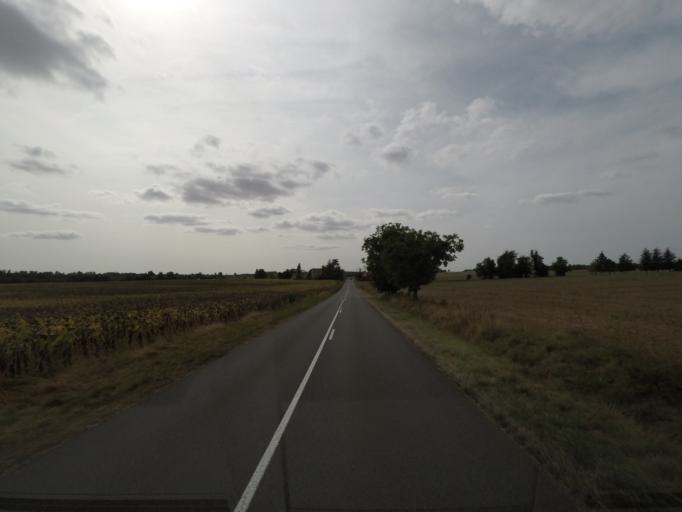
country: FR
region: Poitou-Charentes
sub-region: Departement de la Charente
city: Nanteuil-en-Vallee
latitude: 46.0186
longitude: 0.2829
